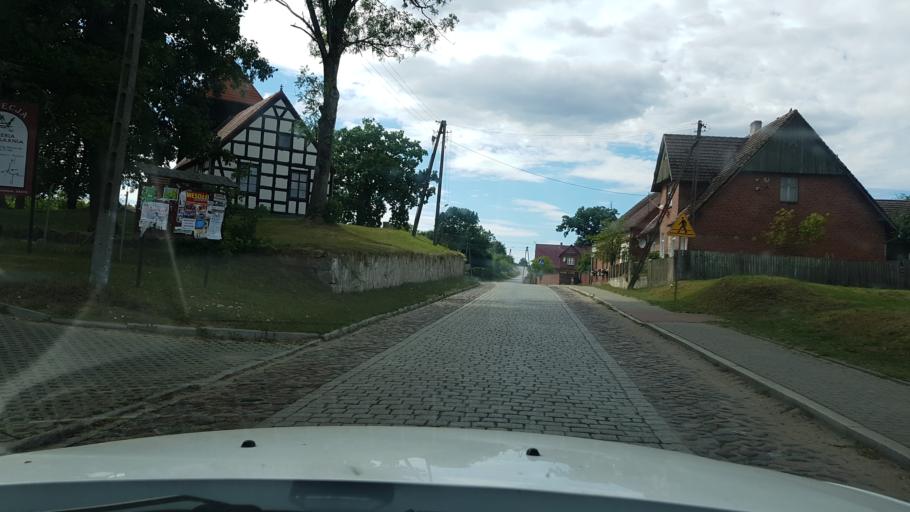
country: PL
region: West Pomeranian Voivodeship
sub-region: Powiat drawski
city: Wierzchowo
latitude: 53.4799
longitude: 16.0514
